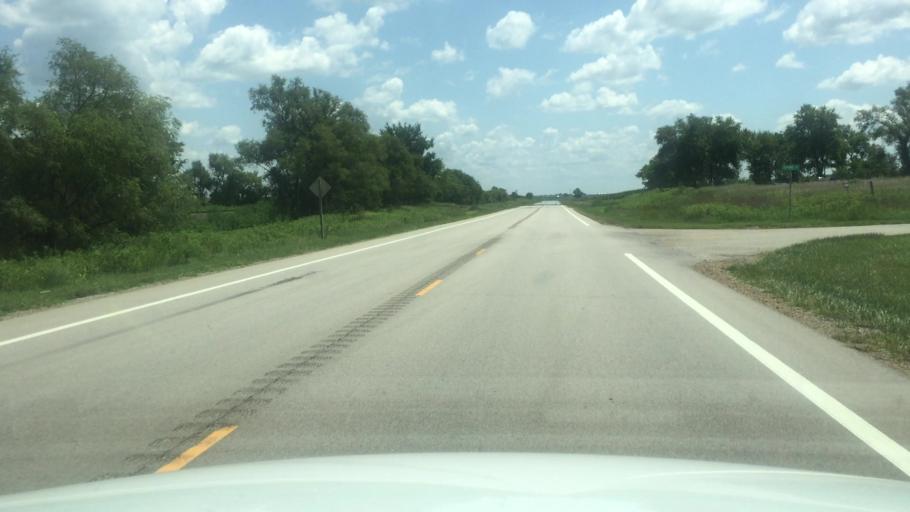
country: US
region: Kansas
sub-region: Brown County
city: Horton
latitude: 39.6036
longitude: -95.3394
